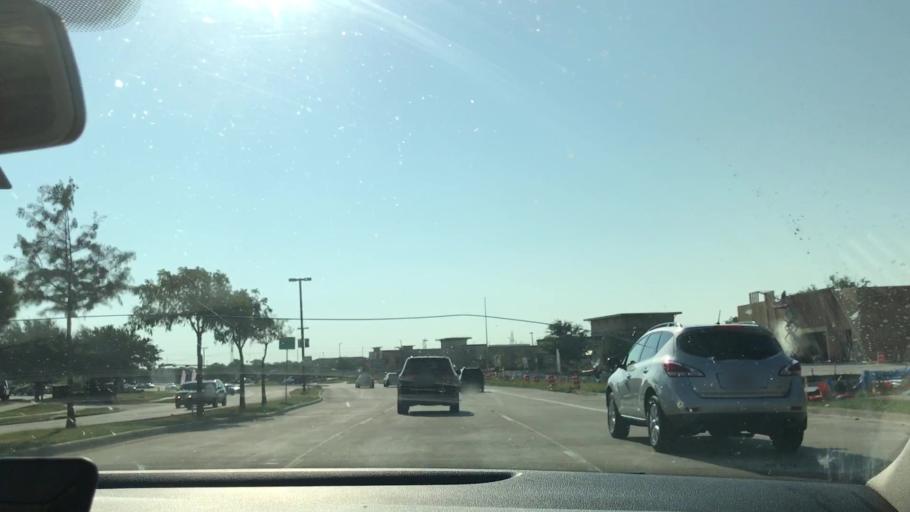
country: US
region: Texas
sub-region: Denton County
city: Lewisville
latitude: 33.0210
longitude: -96.9320
